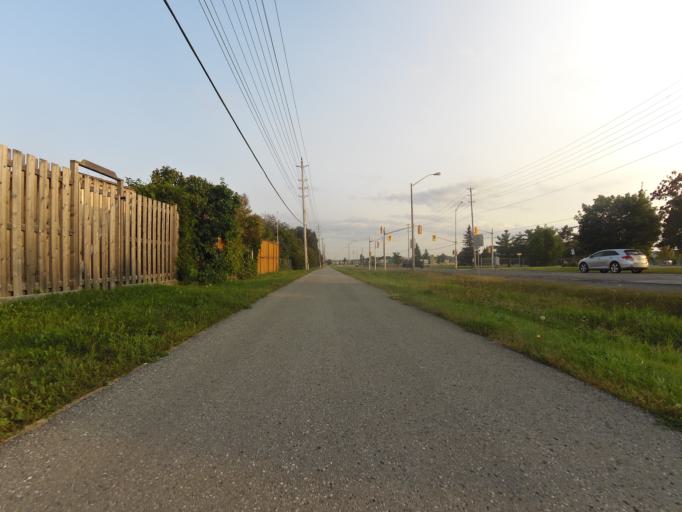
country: CA
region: Ontario
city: Bells Corners
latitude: 45.2774
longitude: -75.7789
